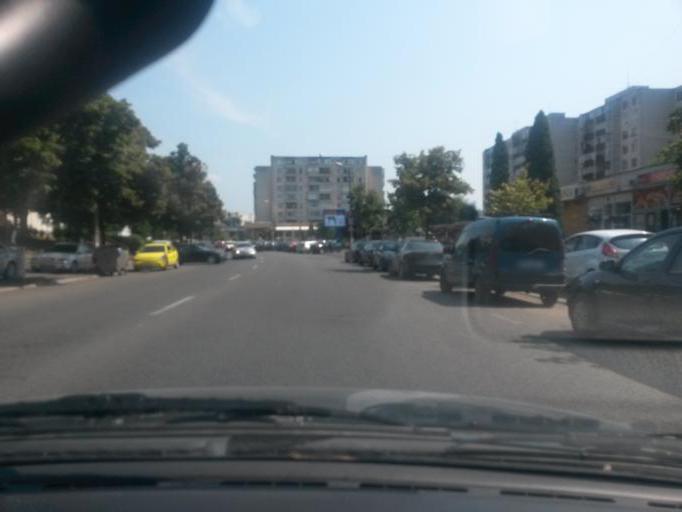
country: RO
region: Mures
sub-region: Comuna Corunca
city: Corunca
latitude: 46.5370
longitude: 24.5908
